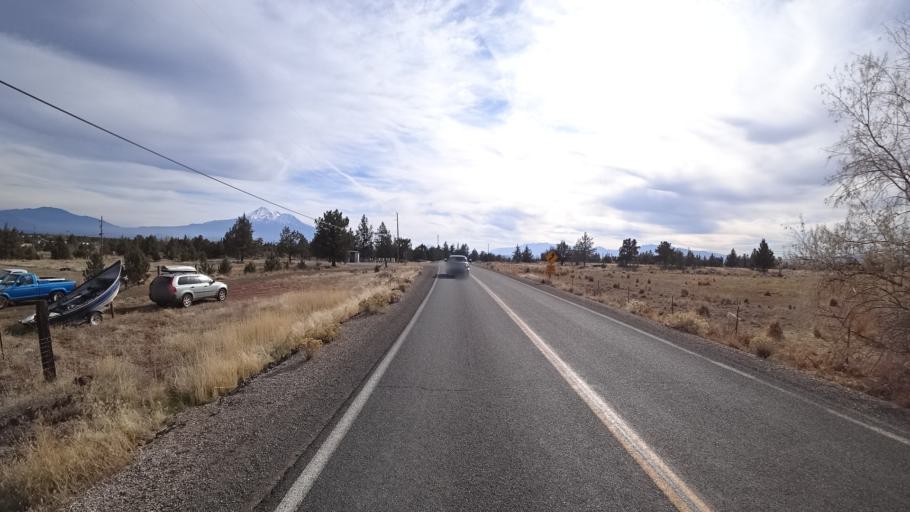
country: US
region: California
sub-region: Siskiyou County
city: Montague
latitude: 41.6443
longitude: -122.3987
